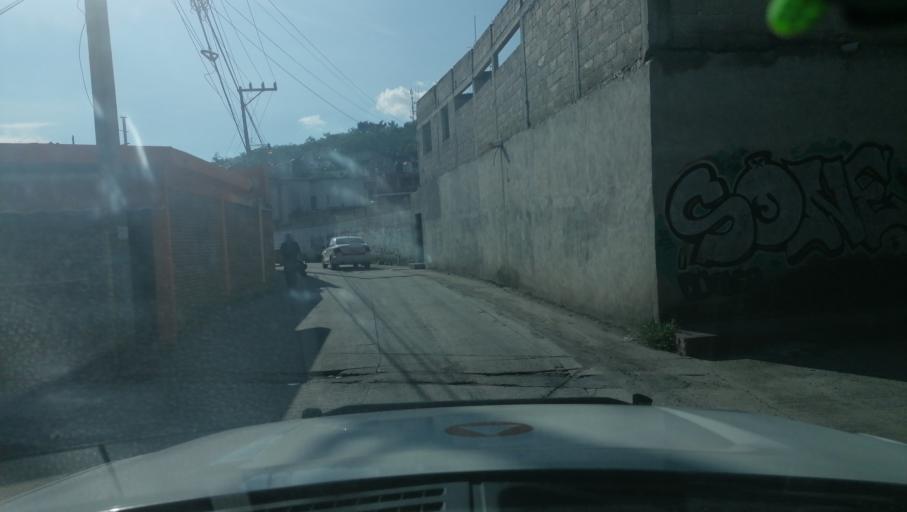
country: MX
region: Morelos
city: Emiliano Zapata
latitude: 18.8371
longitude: -99.1871
